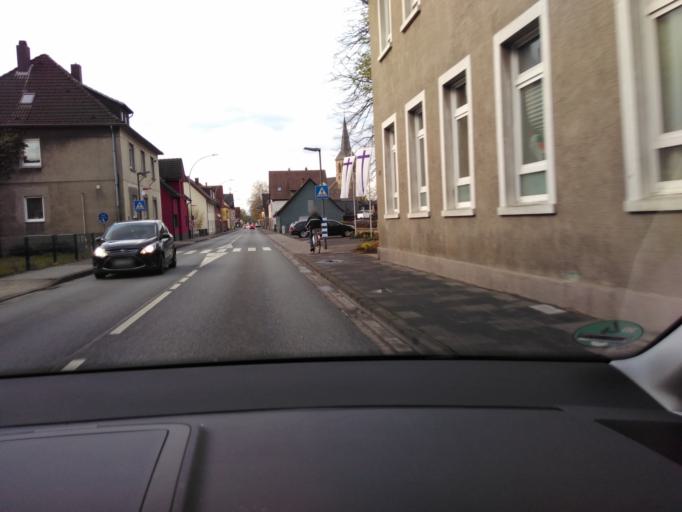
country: DE
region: North Rhine-Westphalia
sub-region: Regierungsbezirk Detmold
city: Verl
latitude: 51.9381
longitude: 8.4871
